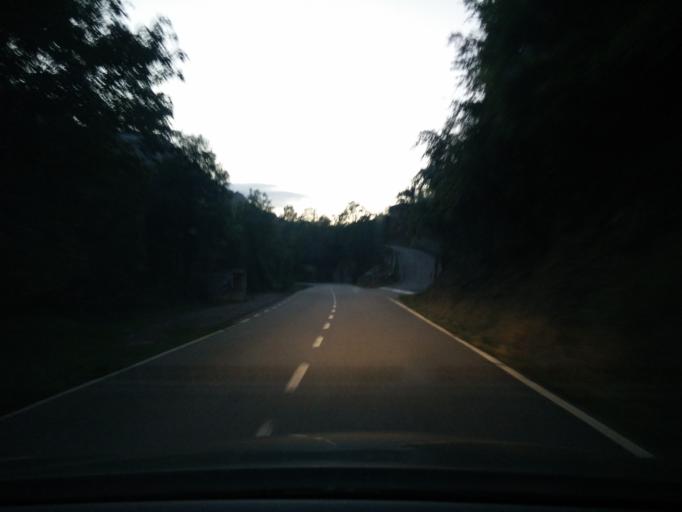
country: ES
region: Asturias
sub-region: Province of Asturias
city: Amieva
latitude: 43.2395
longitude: -5.0945
